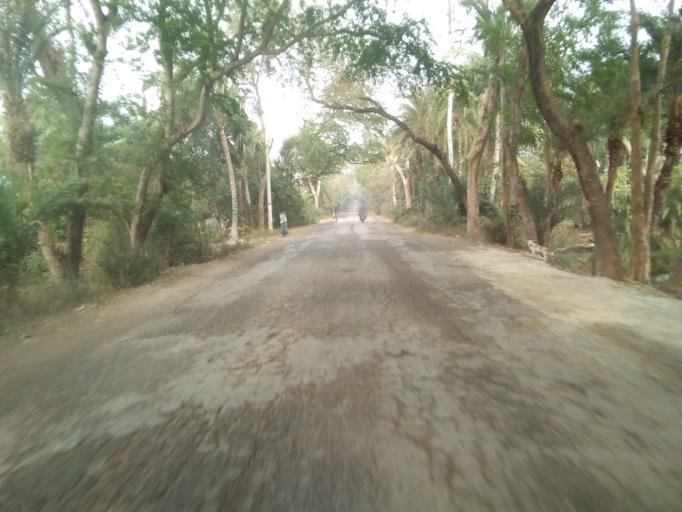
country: BD
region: Khulna
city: Satkhira
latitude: 22.6827
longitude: 89.0267
